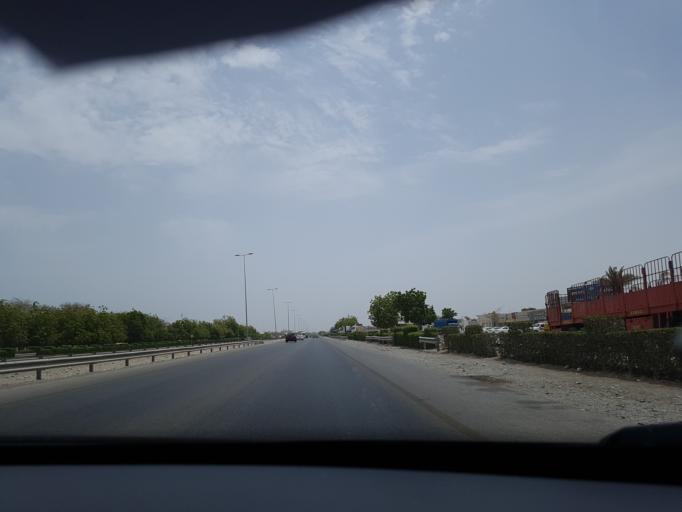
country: OM
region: Muhafazat Masqat
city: As Sib al Jadidah
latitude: 23.6914
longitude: 58.0467
